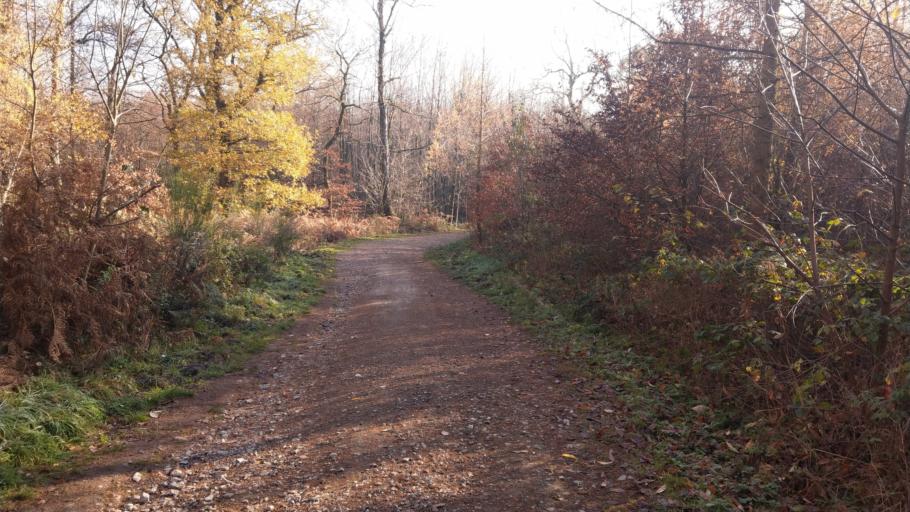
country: BE
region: Wallonia
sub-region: Province de Liege
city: La Calamine
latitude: 50.7351
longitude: 6.0184
